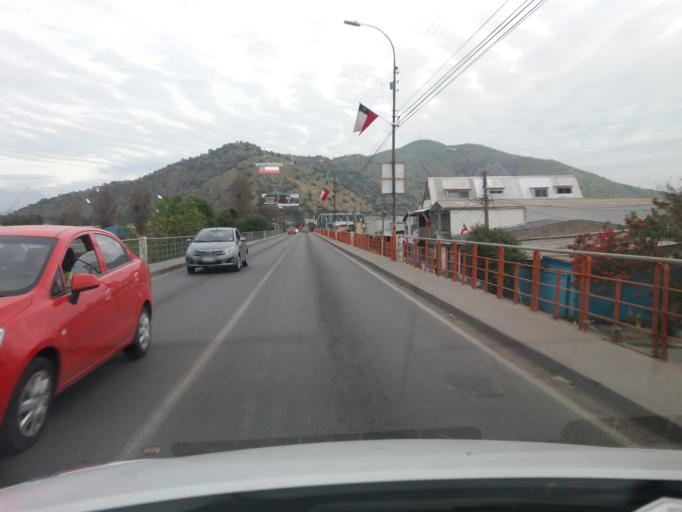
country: CL
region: Valparaiso
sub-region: Provincia de Quillota
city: Hacienda La Calera
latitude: -32.7815
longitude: -71.1909
